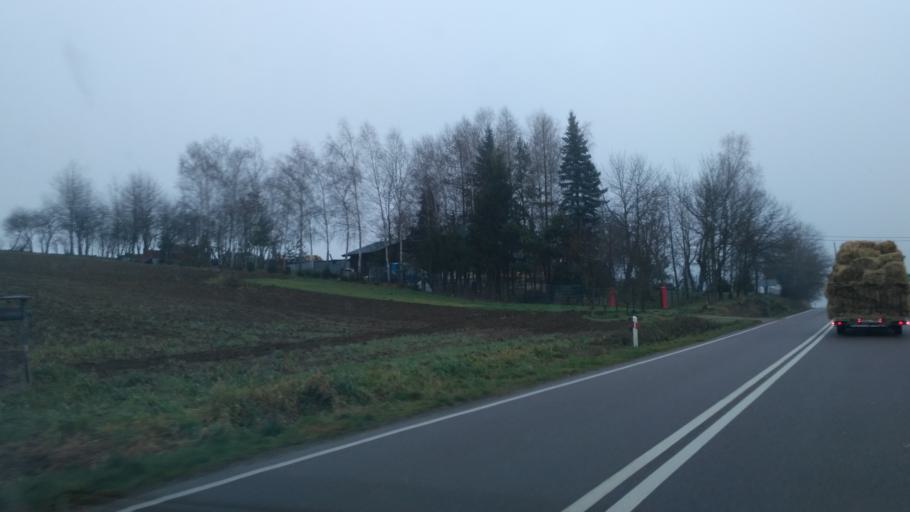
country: PL
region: Subcarpathian Voivodeship
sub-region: Powiat przemyski
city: Przedmiescie Dubieckie
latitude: 49.8261
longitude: 22.3239
